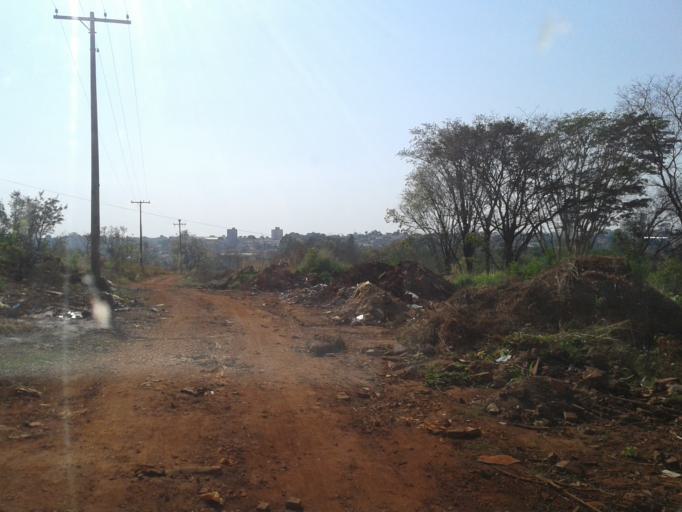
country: BR
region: Minas Gerais
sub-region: Ituiutaba
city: Ituiutaba
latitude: -18.9648
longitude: -49.4790
